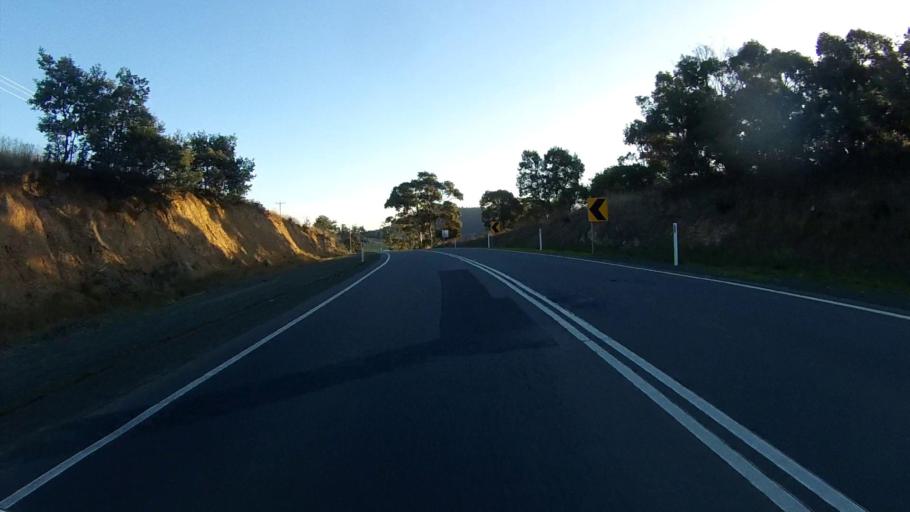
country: AU
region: Tasmania
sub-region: Sorell
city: Sorell
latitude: -42.8134
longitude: 147.7775
